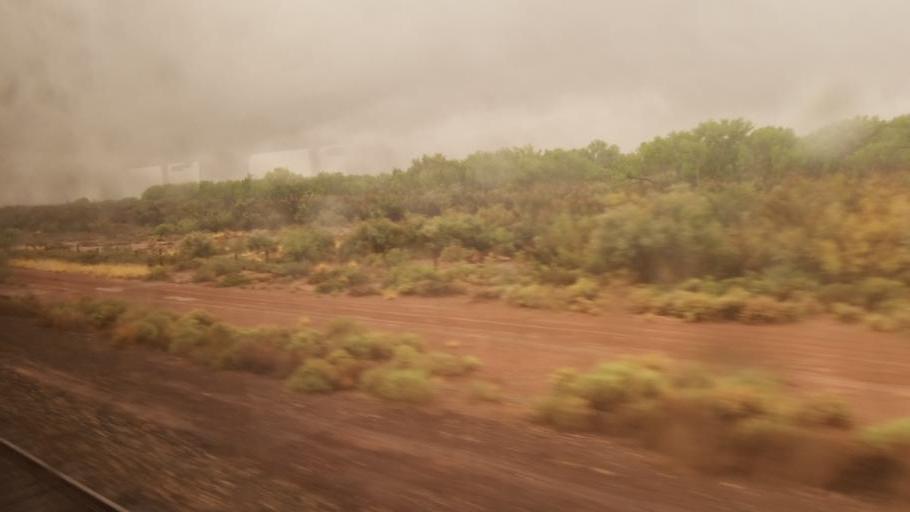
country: US
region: Arizona
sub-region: Navajo County
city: Holbrook
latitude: 34.9034
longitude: -110.2309
